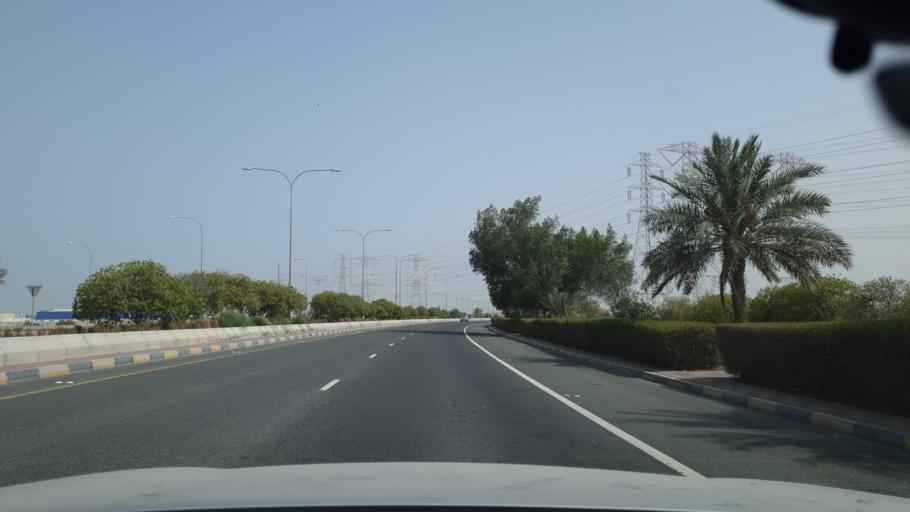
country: QA
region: Al Wakrah
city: Umm Sa'id
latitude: 25.0063
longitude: 51.5595
